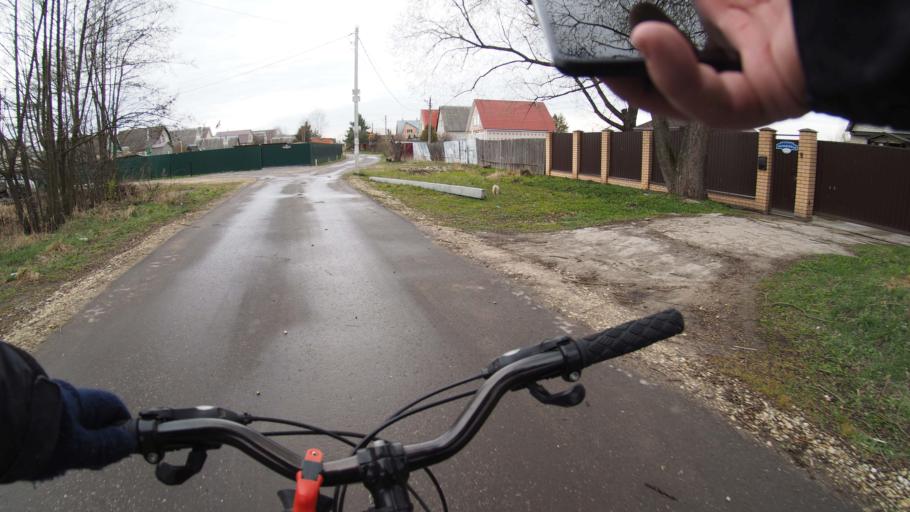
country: RU
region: Moskovskaya
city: Malyshevo
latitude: 55.5342
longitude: 38.3275
